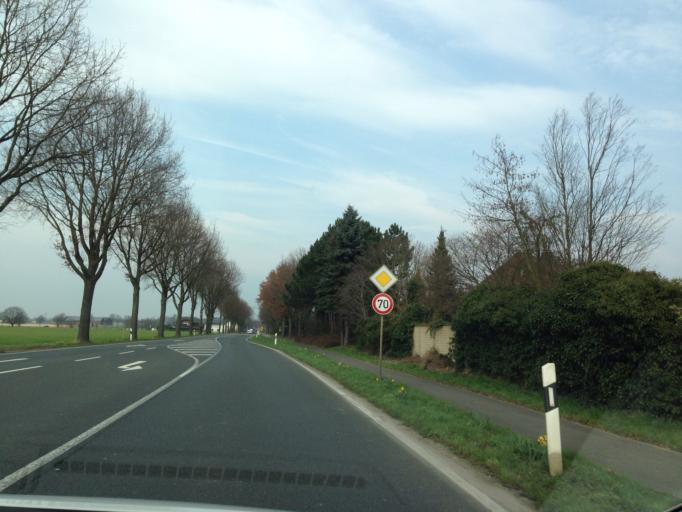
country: DE
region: North Rhine-Westphalia
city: Erkelenz
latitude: 51.0529
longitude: 6.2898
